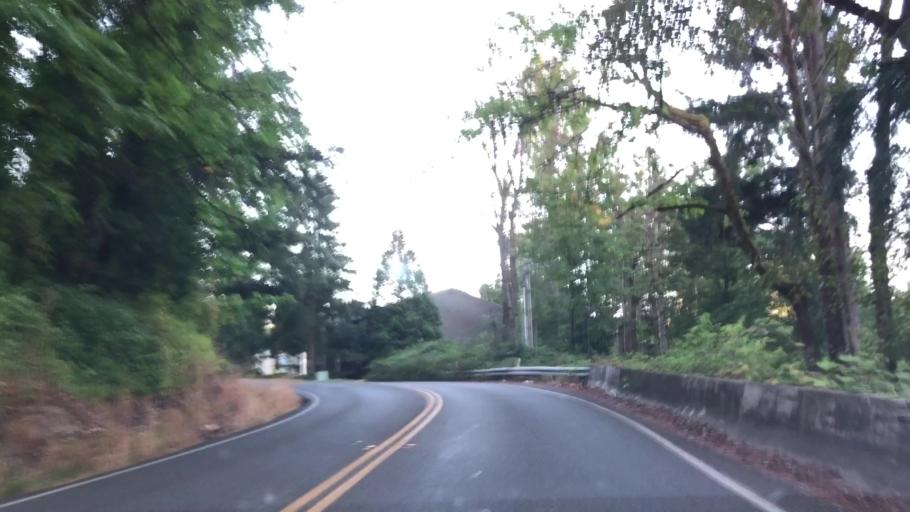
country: US
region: Washington
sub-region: King County
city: Lea Hill
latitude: 47.3161
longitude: -122.2007
